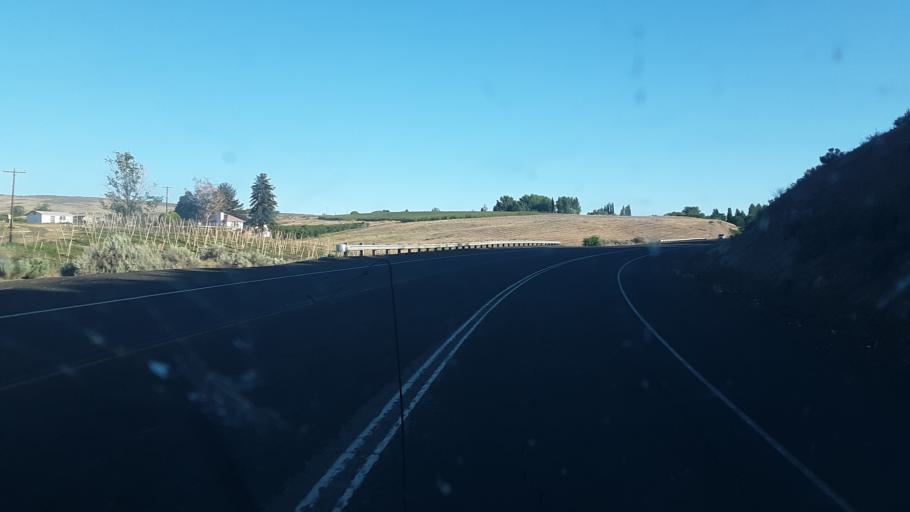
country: US
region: Washington
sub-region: Yakima County
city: West Valley
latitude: 46.6159
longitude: -120.6694
